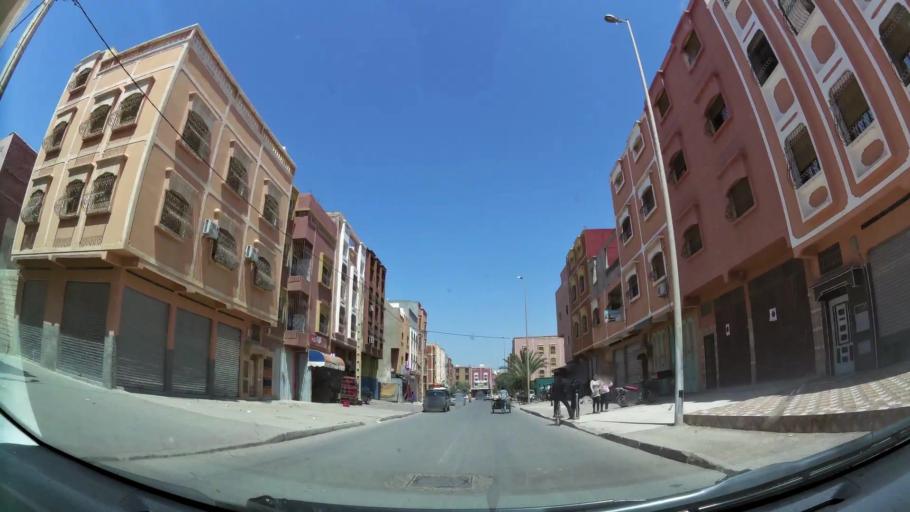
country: MA
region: Souss-Massa-Draa
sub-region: Inezgane-Ait Mellou
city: Inezgane
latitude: 30.3300
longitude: -9.4974
